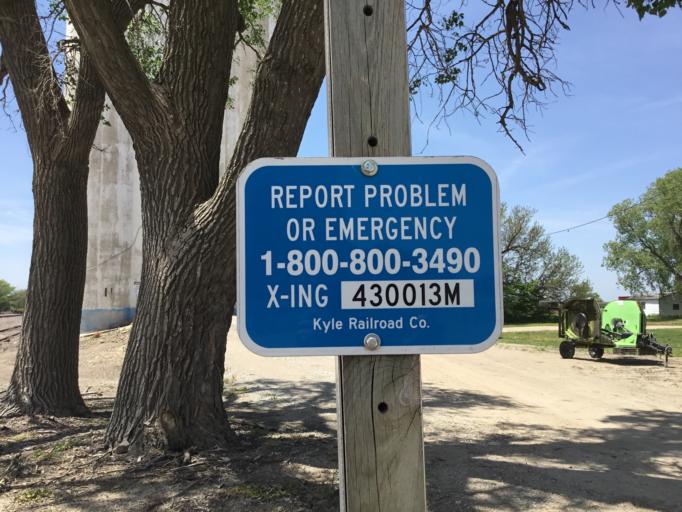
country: US
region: Kansas
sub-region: Mitchell County
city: Beloit
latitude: 39.5438
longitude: -97.9544
